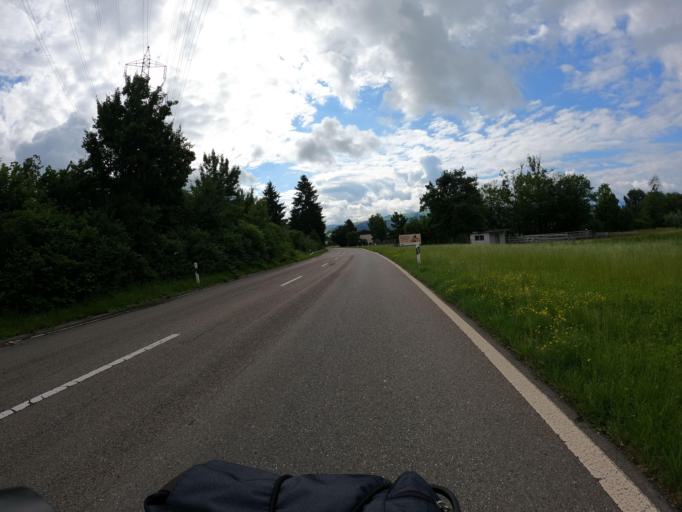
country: CH
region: Zug
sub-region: Zug
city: Steinhausen
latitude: 47.1904
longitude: 8.4850
